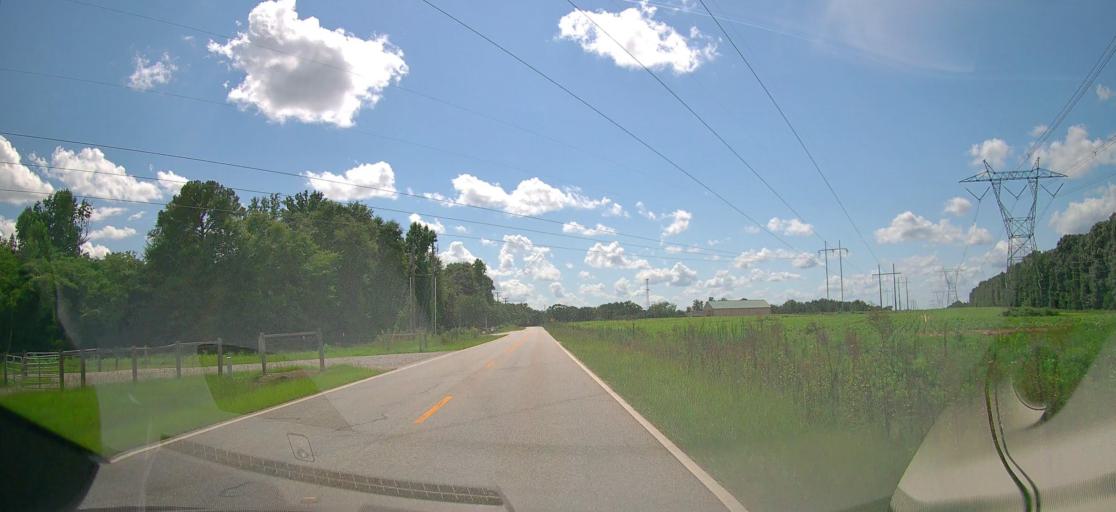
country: US
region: Georgia
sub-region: Houston County
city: Centerville
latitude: 32.6185
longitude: -83.7283
